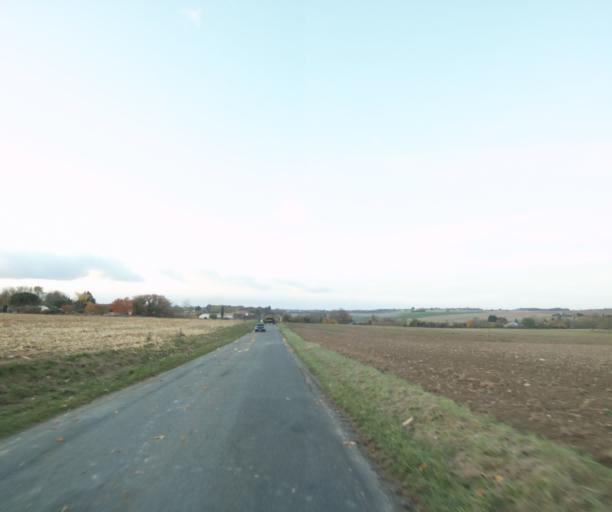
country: FR
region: Poitou-Charentes
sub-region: Departement de la Charente-Maritime
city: Saintes
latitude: 45.7643
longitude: -0.6533
